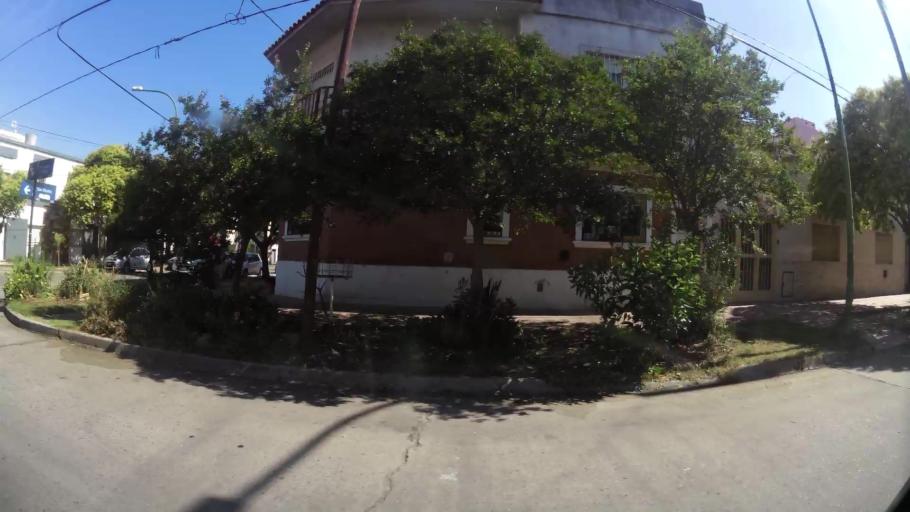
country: AR
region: Cordoba
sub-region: Departamento de Capital
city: Cordoba
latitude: -31.4181
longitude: -64.1683
